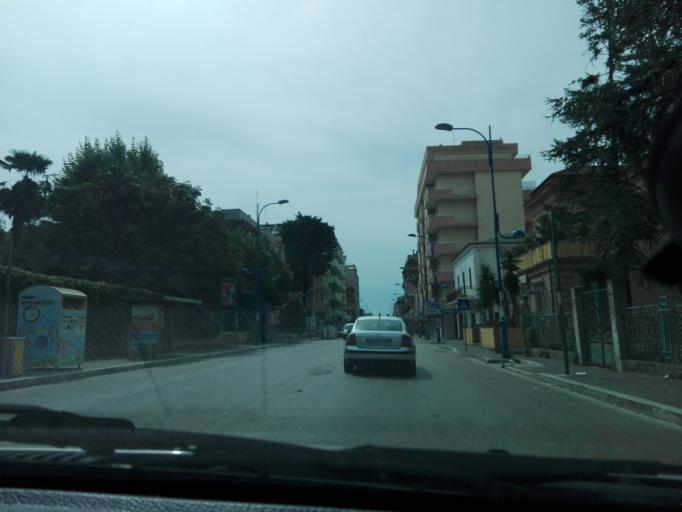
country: IT
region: Abruzzo
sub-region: Provincia di Pescara
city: Montesilvano Marina
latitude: 42.5139
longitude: 14.1528
